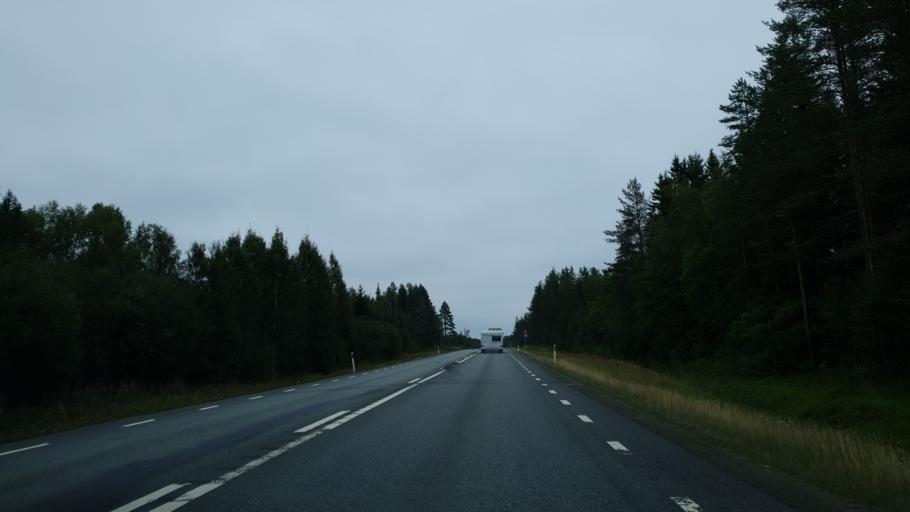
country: SE
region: Vaesterbotten
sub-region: Skelleftea Kommun
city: Burea
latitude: 64.3421
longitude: 21.2807
